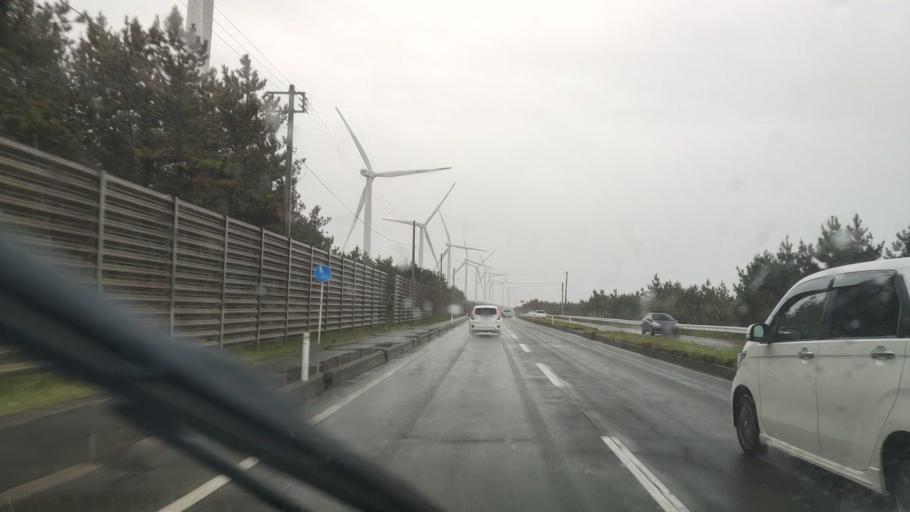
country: JP
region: Akita
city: Tenno
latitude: 39.8215
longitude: 140.0261
